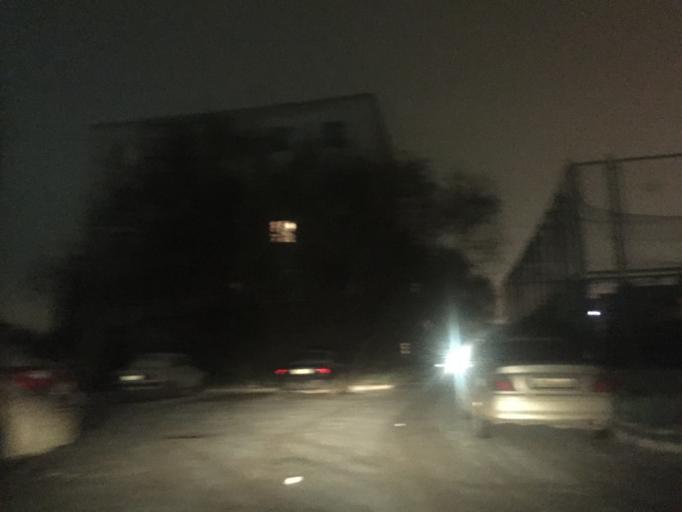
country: KZ
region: Astana Qalasy
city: Astana
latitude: 51.1895
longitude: 71.4218
